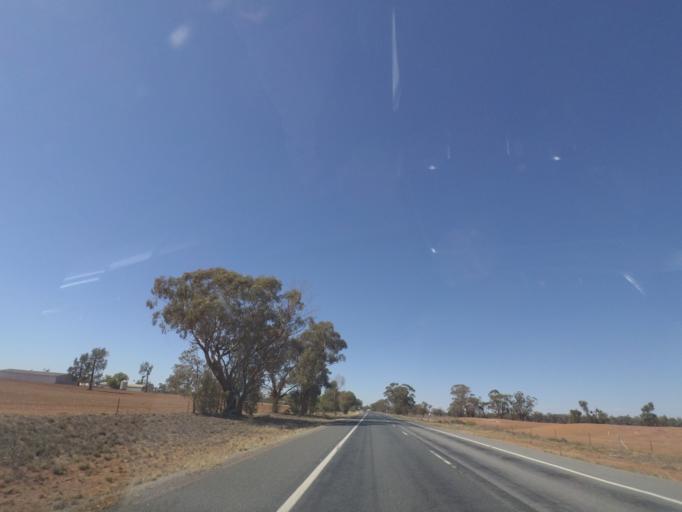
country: AU
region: New South Wales
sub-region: Bland
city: West Wyalong
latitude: -34.1902
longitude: 147.1118
